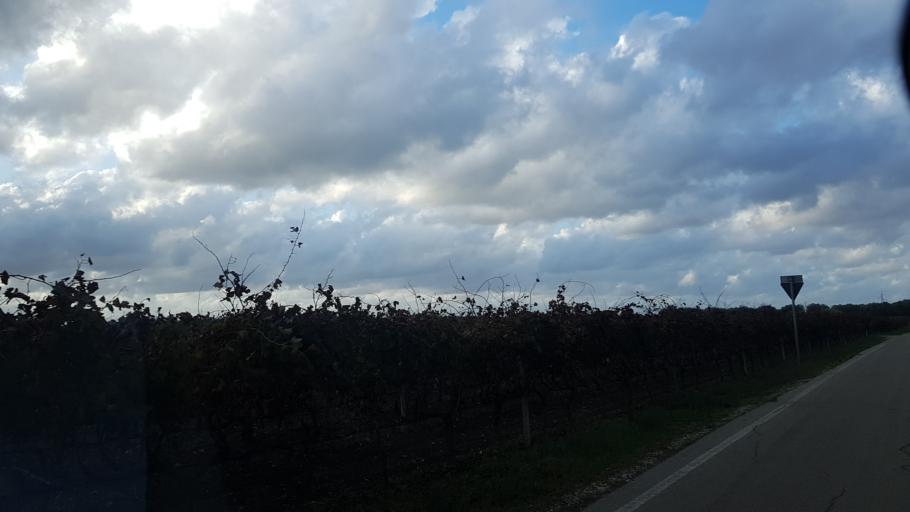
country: IT
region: Apulia
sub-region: Provincia di Brindisi
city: San Pietro Vernotico
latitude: 40.5091
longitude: 18.0207
